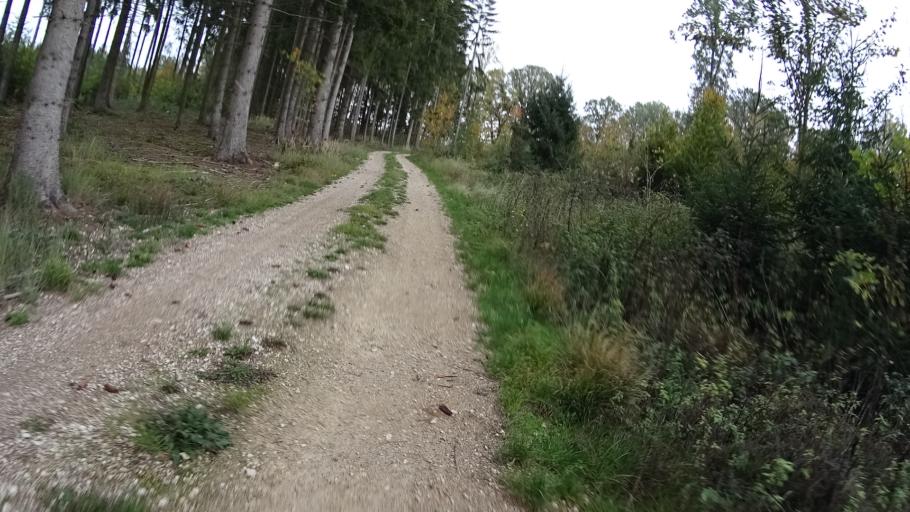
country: DE
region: Bavaria
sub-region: Upper Bavaria
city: Hitzhofen
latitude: 48.8386
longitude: 11.2980
